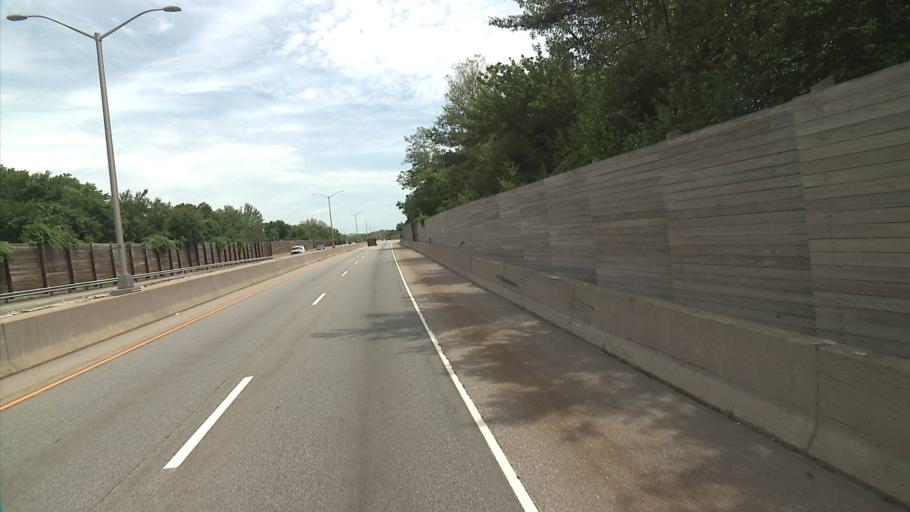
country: US
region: Connecticut
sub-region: New London County
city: Montville Center
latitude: 41.4858
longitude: -72.1064
